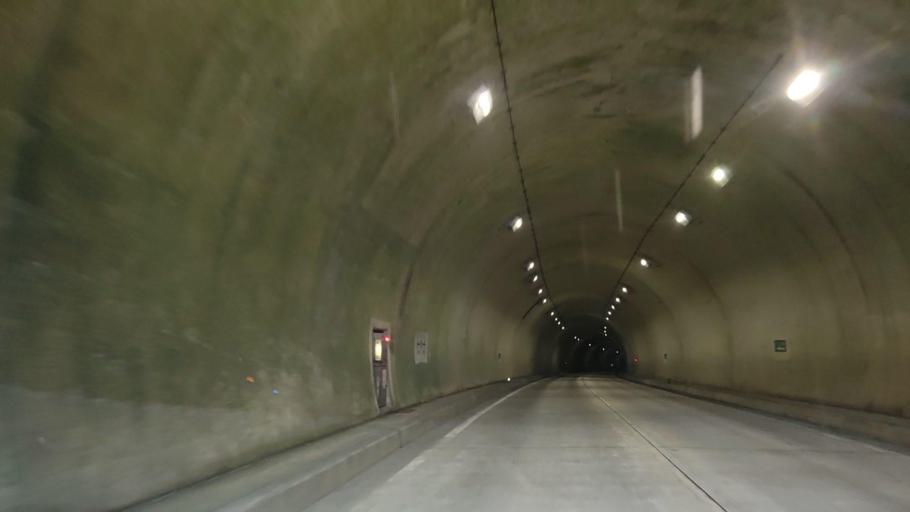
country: JP
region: Tottori
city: Yonago
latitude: 35.2696
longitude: 133.4349
